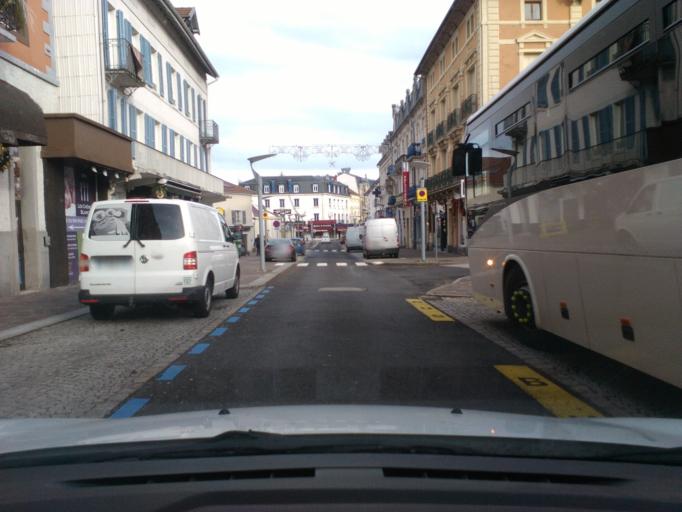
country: FR
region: Lorraine
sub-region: Departement des Vosges
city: Gerardmer
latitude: 48.0691
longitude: 6.8741
